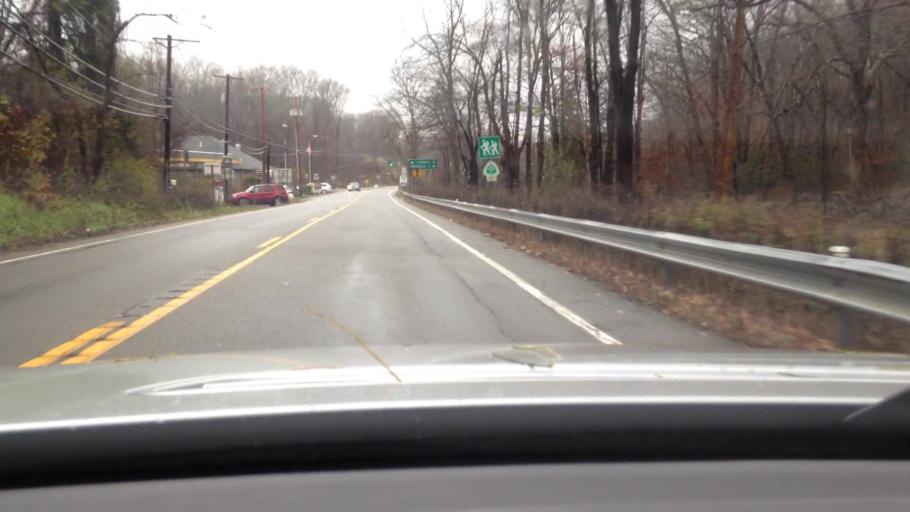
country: US
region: New York
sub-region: Orange County
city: Highland Falls
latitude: 41.3525
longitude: -73.9258
